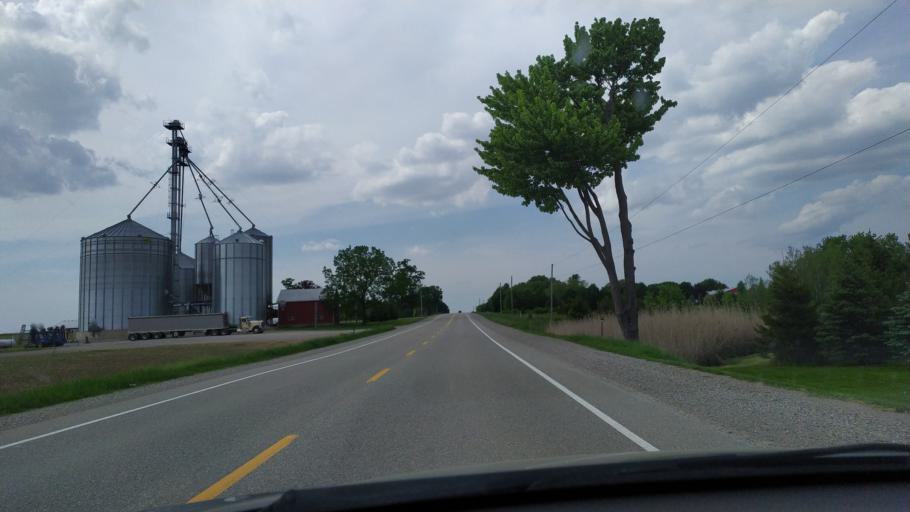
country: CA
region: Ontario
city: Dorchester
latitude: 43.1681
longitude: -81.0449
